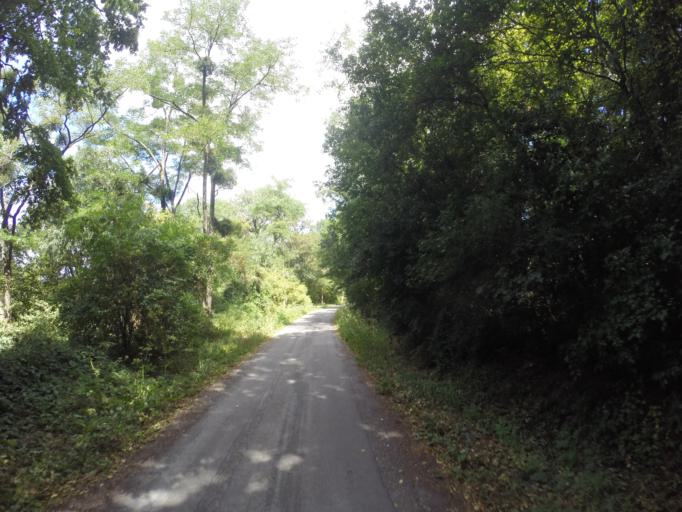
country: FR
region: Centre
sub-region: Departement d'Indre-et-Loire
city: Rochecorbon
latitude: 47.4164
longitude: 0.7170
